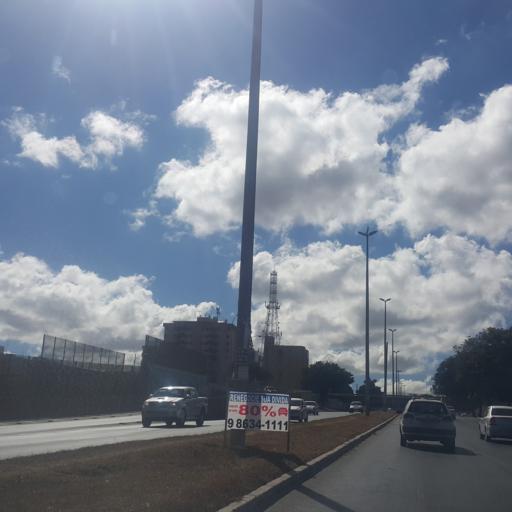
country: BR
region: Federal District
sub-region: Brasilia
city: Brasilia
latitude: -15.8355
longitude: -48.0624
